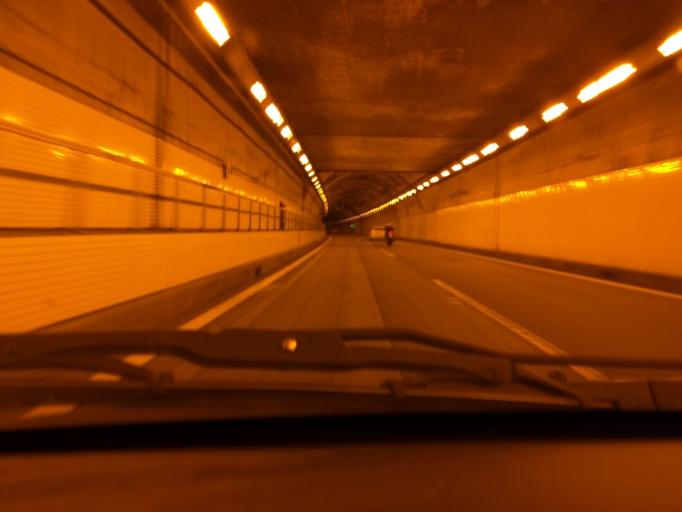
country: JP
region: Niigata
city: Ojiya
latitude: 37.2766
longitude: 138.7920
